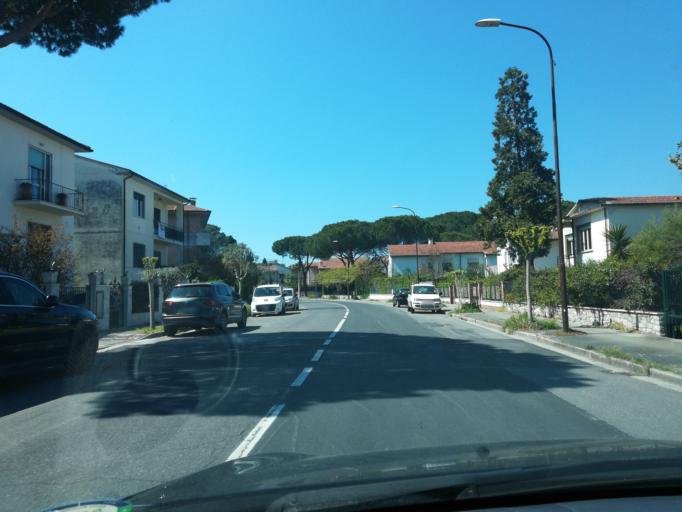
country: IT
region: Tuscany
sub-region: Province of Pisa
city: Pisa
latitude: 43.7334
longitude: 10.4057
